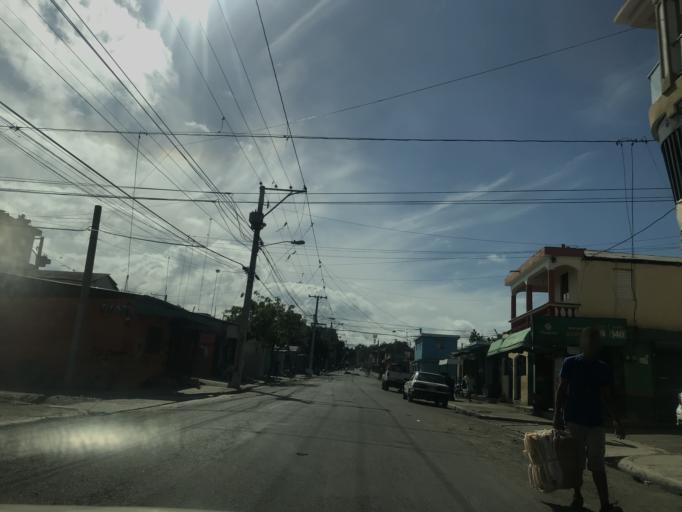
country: DO
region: Santiago
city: Palmar Arriba
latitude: 19.4815
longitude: -70.7495
